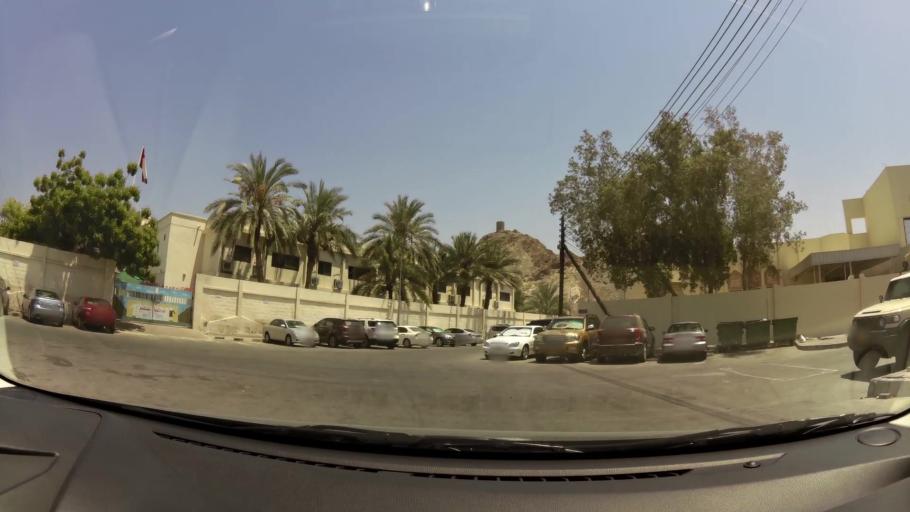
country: OM
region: Muhafazat Masqat
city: Muscat
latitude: 23.6219
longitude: 58.5592
